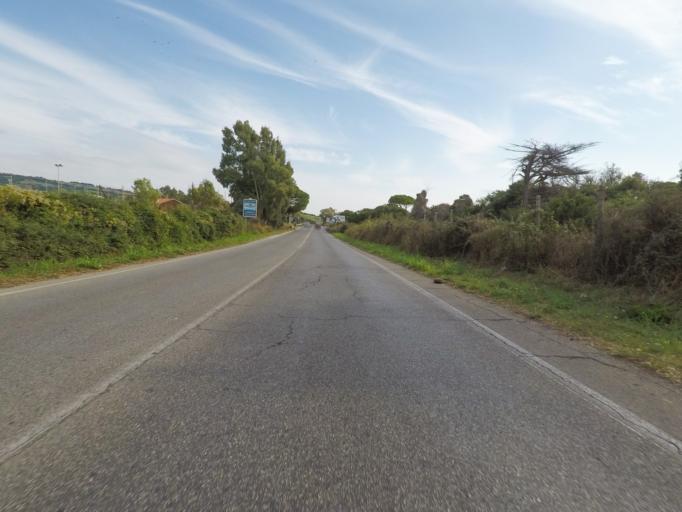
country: IT
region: Latium
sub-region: Citta metropolitana di Roma Capitale
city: Civitavecchia
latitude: 42.0589
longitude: 11.8175
